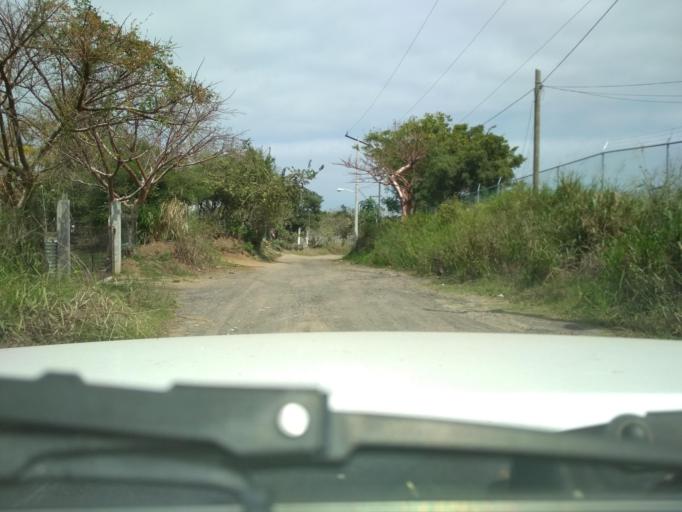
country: MX
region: Veracruz
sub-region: Veracruz
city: Delfino Victoria (Santa Fe)
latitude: 19.2517
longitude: -96.2650
